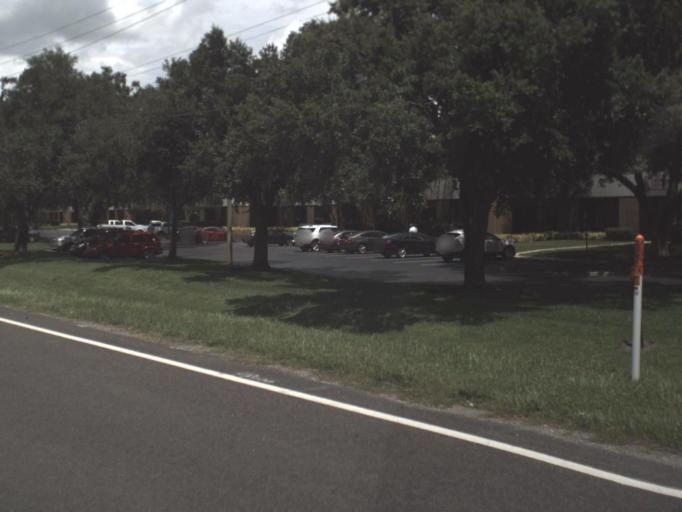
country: US
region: Florida
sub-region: Hillsborough County
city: East Lake-Orient Park
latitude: 27.9605
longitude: -82.3589
